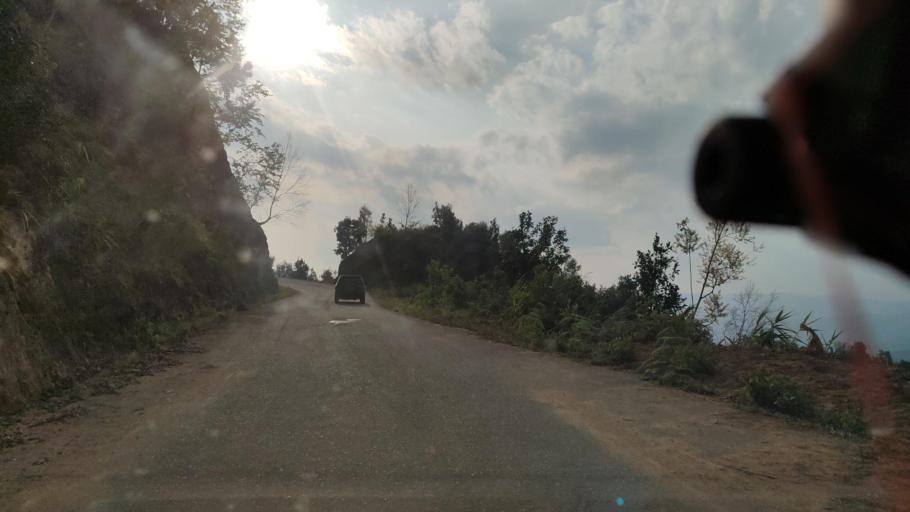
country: CN
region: Yunnan
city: Menghai
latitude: 21.4632
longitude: 99.7072
